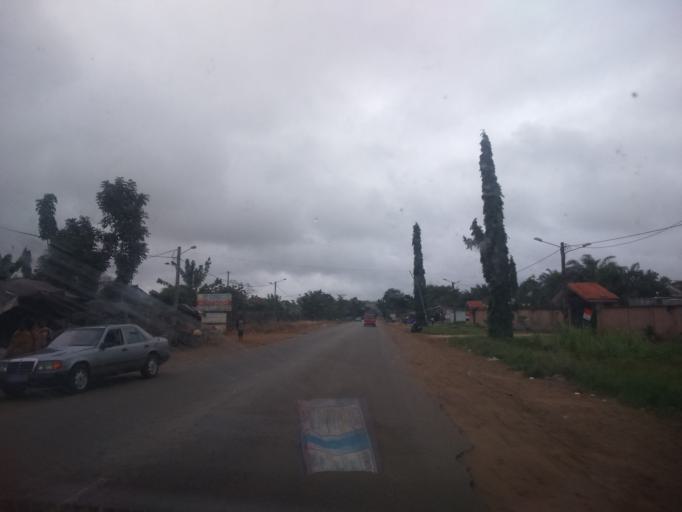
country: CI
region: Sud-Comoe
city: Bonoua
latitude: 5.2455
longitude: -3.6248
